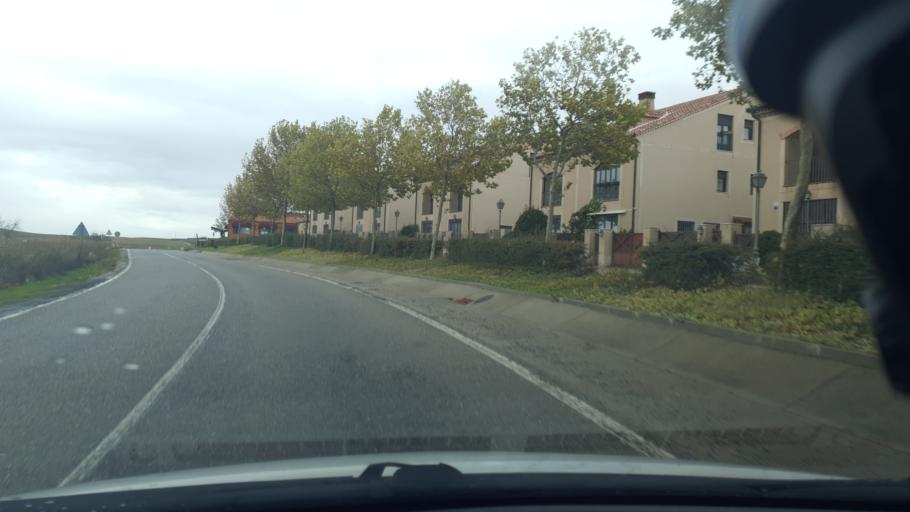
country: ES
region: Castille and Leon
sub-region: Provincia de Segovia
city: Segovia
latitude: 40.9631
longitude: -4.1352
